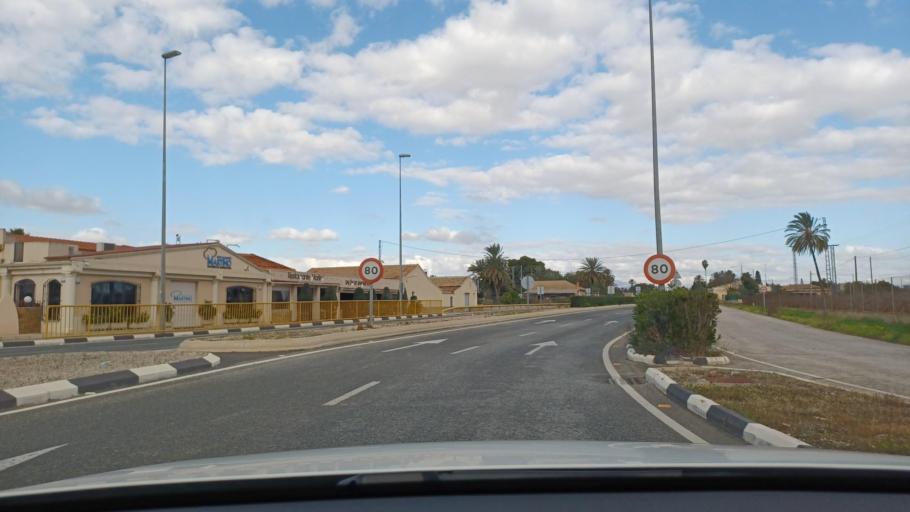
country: ES
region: Valencia
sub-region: Provincia de Alicante
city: Elche
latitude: 38.1955
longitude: -0.7005
